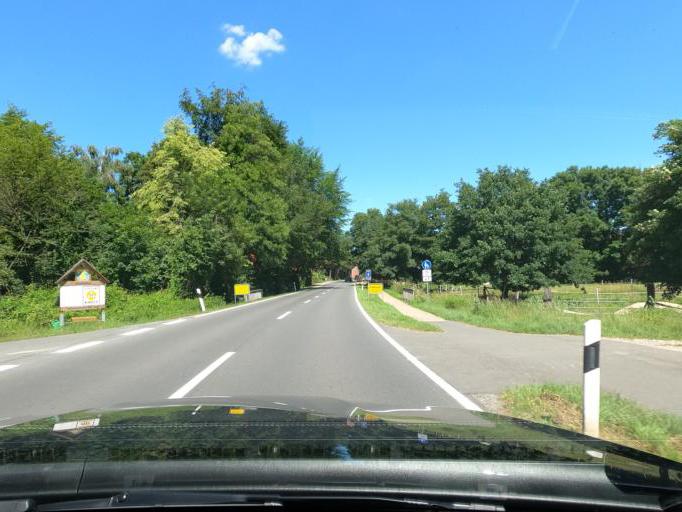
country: DE
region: Lower Saxony
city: Lehrte
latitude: 52.4144
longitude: 9.9771
